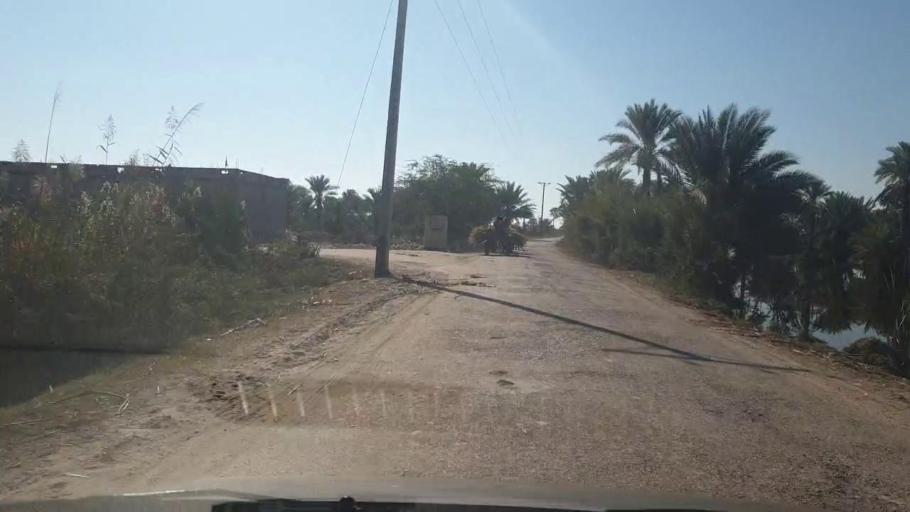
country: PK
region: Sindh
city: Bozdar
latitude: 27.2441
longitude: 68.6522
